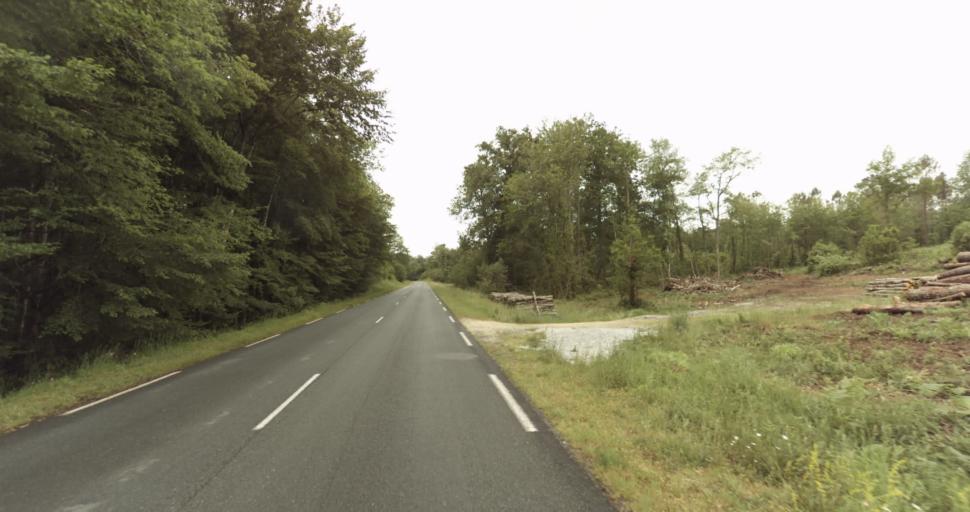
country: FR
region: Aquitaine
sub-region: Departement de la Dordogne
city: Belves
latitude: 44.6814
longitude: 0.9911
